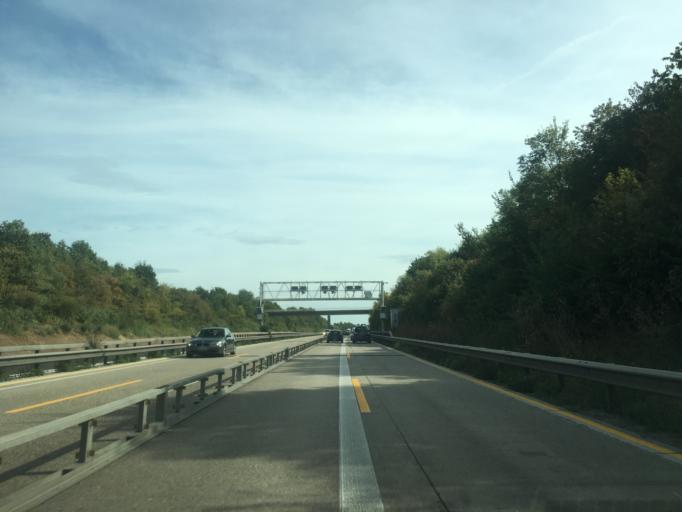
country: DE
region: Rheinland-Pfalz
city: Morstadt
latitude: 49.6541
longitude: 8.2866
